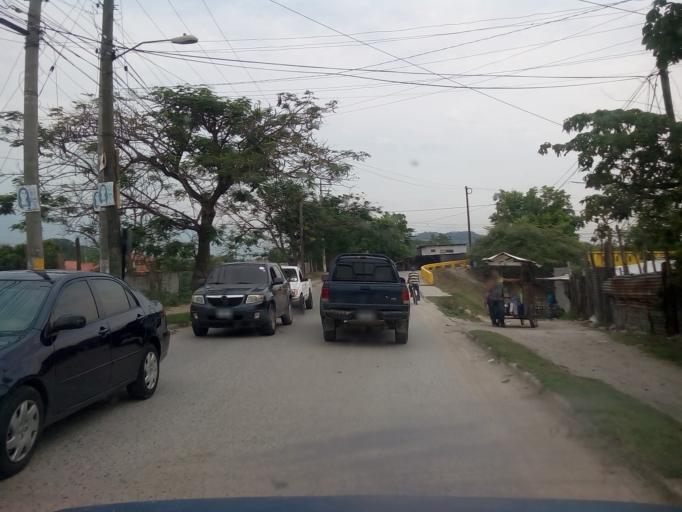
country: HN
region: Cortes
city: San Pedro Sula
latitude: 15.5008
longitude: -87.9848
